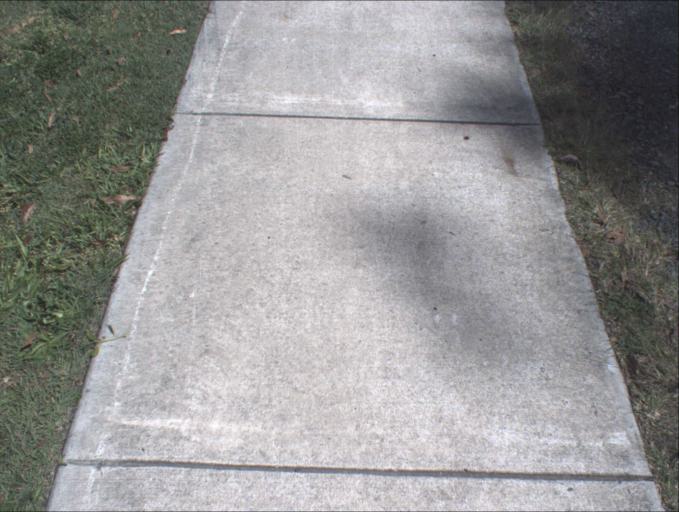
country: AU
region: Queensland
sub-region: Logan
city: Park Ridge South
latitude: -27.7290
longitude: 153.0441
